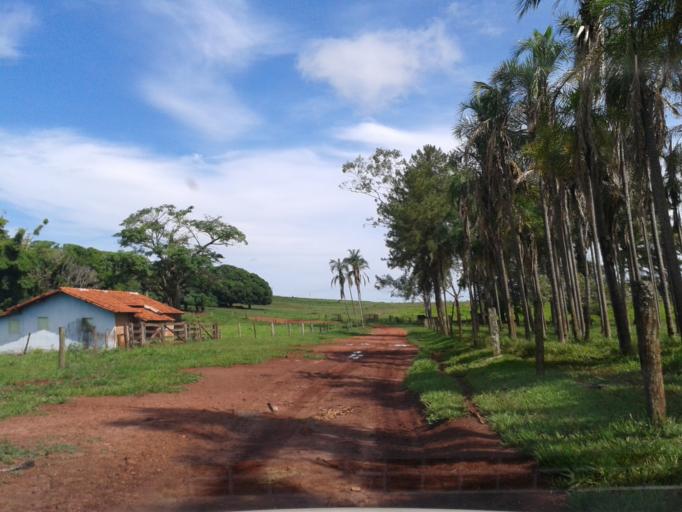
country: BR
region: Minas Gerais
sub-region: Santa Vitoria
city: Santa Vitoria
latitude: -19.2068
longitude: -50.6828
